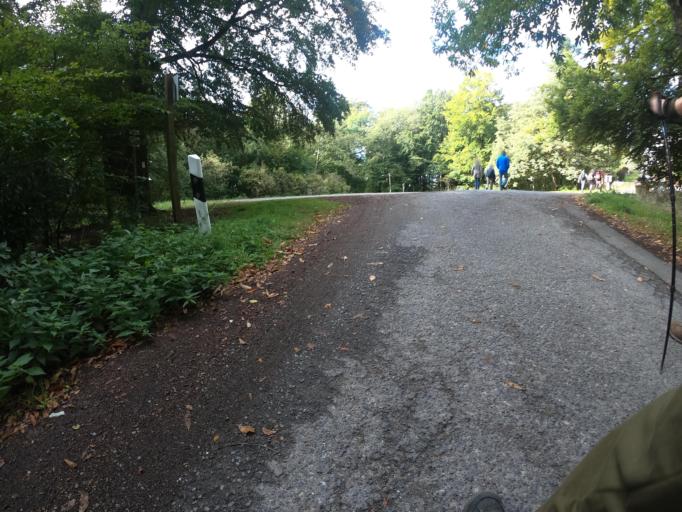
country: DE
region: Hesse
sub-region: Regierungsbezirk Darmstadt
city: Niedernhausen
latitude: 50.1378
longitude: 8.2846
